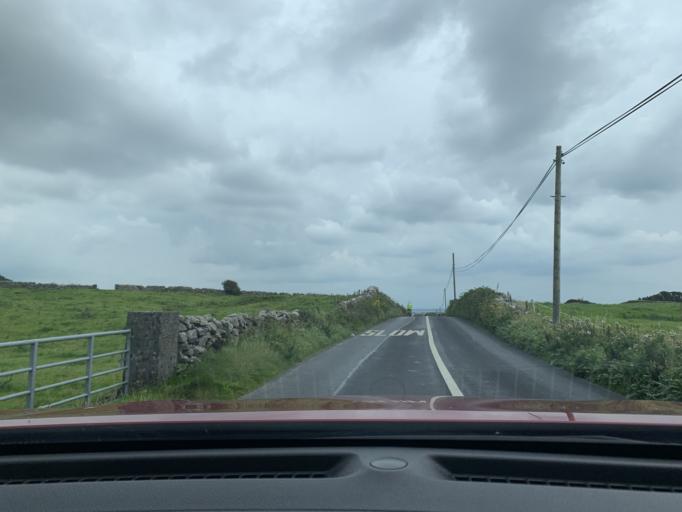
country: IE
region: Connaught
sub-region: County Galway
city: Bearna
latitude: 53.2796
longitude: -9.1103
